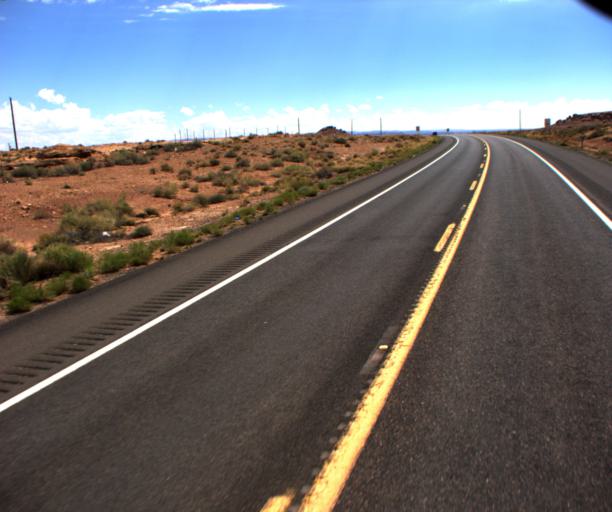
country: US
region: Arizona
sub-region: Coconino County
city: Tuba City
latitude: 35.8559
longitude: -111.4395
